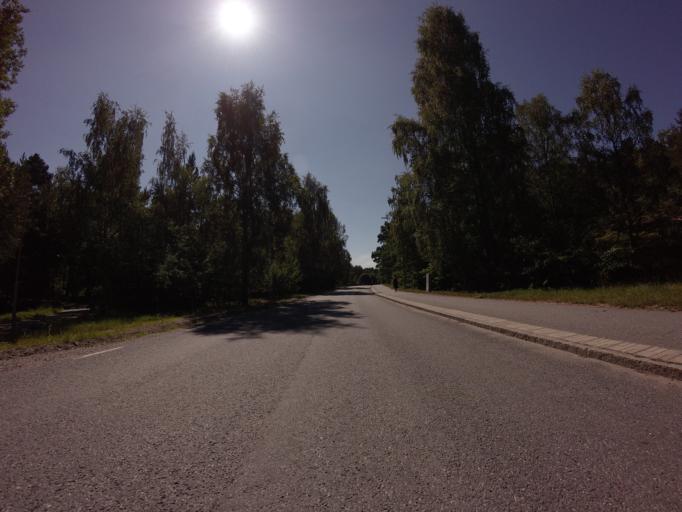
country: SE
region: Stockholm
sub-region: Lidingo
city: Brevik
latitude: 59.3577
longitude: 18.2232
